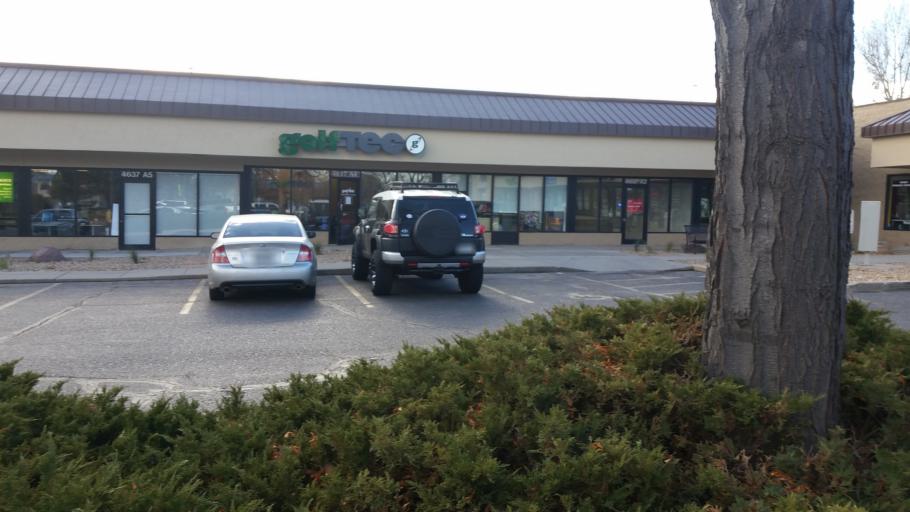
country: US
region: Colorado
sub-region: Larimer County
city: Fort Collins
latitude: 40.5214
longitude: -105.0785
